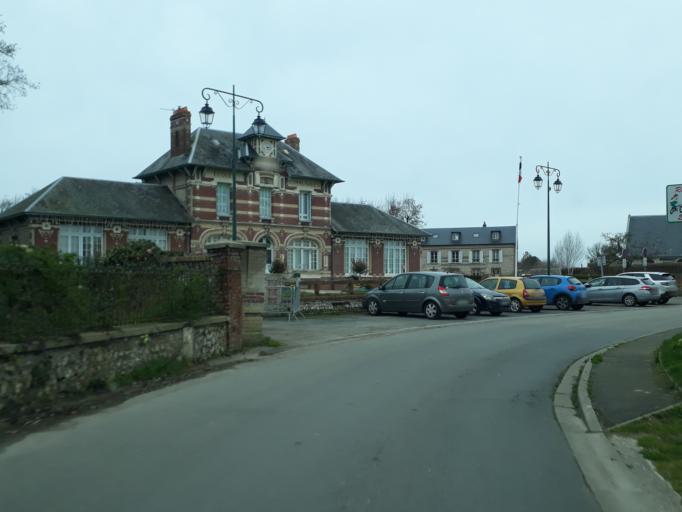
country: FR
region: Haute-Normandie
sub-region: Departement de la Seine-Maritime
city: Les Loges
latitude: 49.7272
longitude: 0.2799
